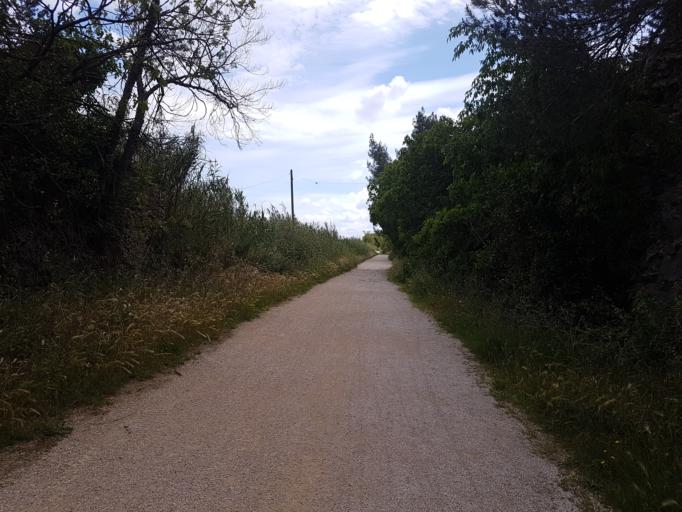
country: FR
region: Languedoc-Roussillon
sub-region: Departement du Gard
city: Beaucaire
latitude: 43.8217
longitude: 4.6283
